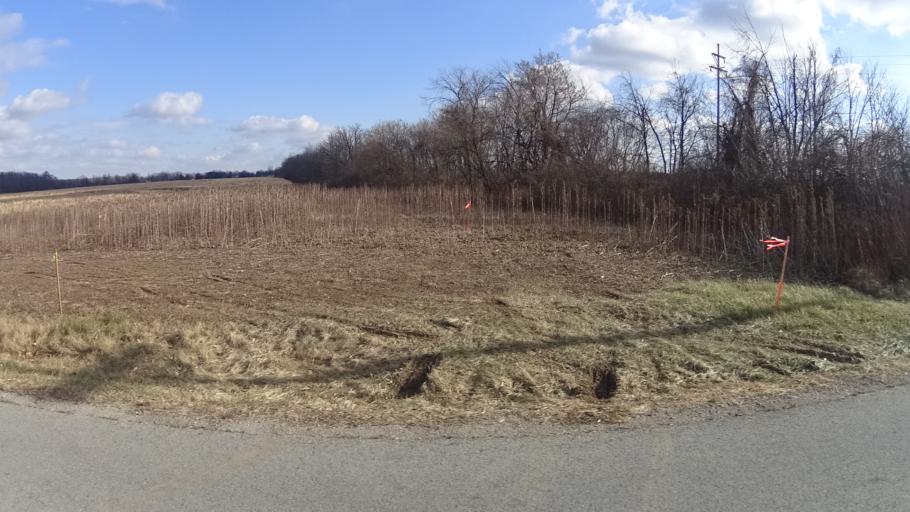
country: US
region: Ohio
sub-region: Lorain County
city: Camden
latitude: 41.2710
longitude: -82.2889
